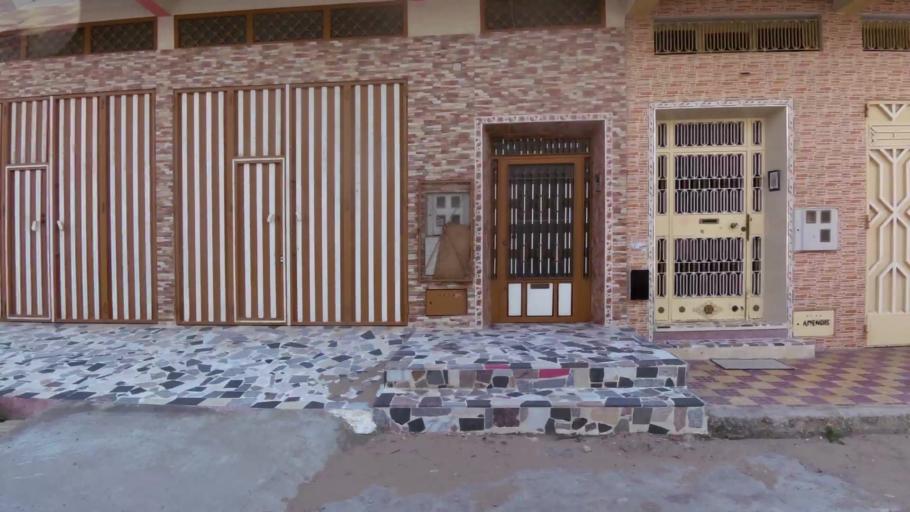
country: MA
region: Tanger-Tetouan
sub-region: Tanger-Assilah
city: Tangier
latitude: 35.7432
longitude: -5.8367
